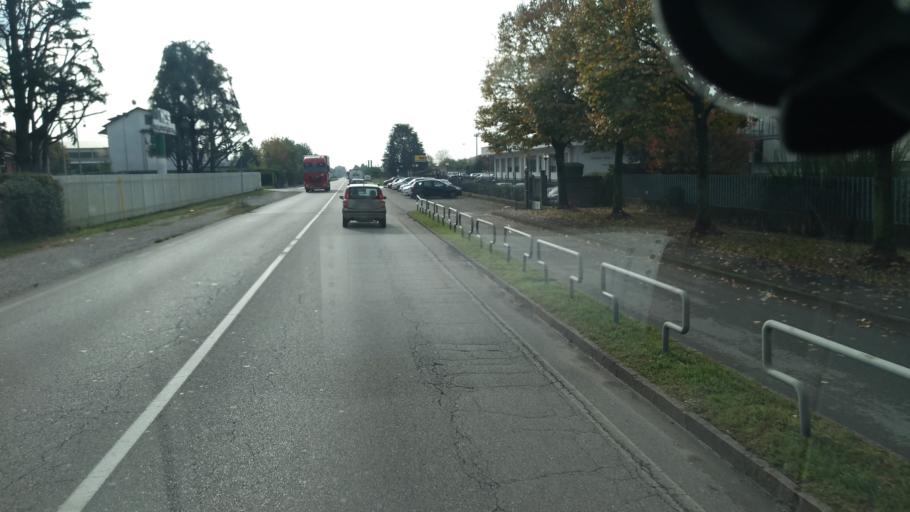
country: IT
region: Lombardy
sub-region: Provincia di Bergamo
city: Urgnano
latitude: 45.6123
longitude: 9.6943
